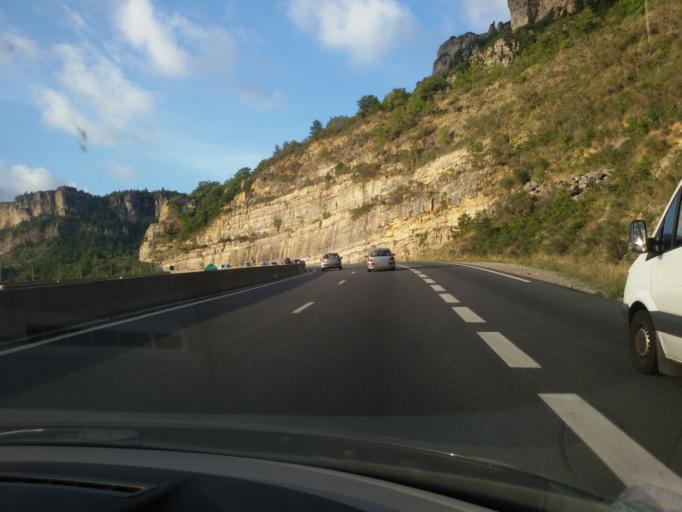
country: FR
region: Languedoc-Roussillon
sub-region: Departement de l'Herault
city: Lodeve
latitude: 43.8168
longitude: 3.3188
